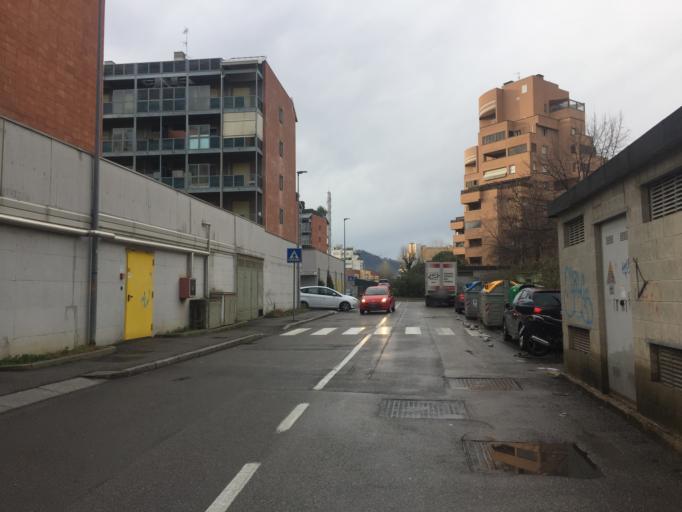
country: IT
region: Emilia-Romagna
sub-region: Provincia di Bologna
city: Bologna
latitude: 44.5055
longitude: 11.3046
